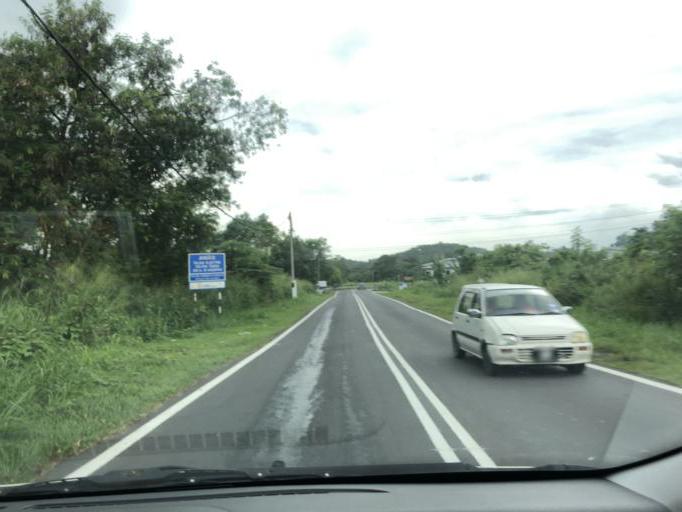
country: MY
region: Putrajaya
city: Putrajaya
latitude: 2.9181
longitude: 101.7552
